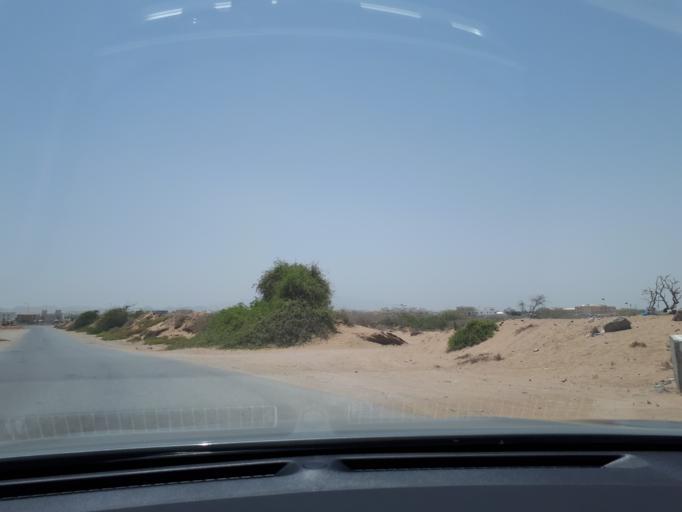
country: OM
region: Muhafazat Masqat
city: As Sib al Jadidah
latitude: 23.6308
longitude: 58.2587
